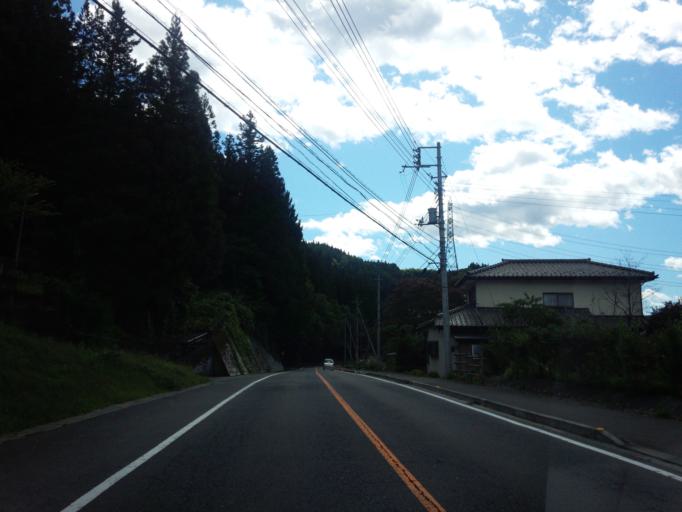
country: JP
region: Gunma
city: Nakanojomachi
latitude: 36.6269
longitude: 138.7959
